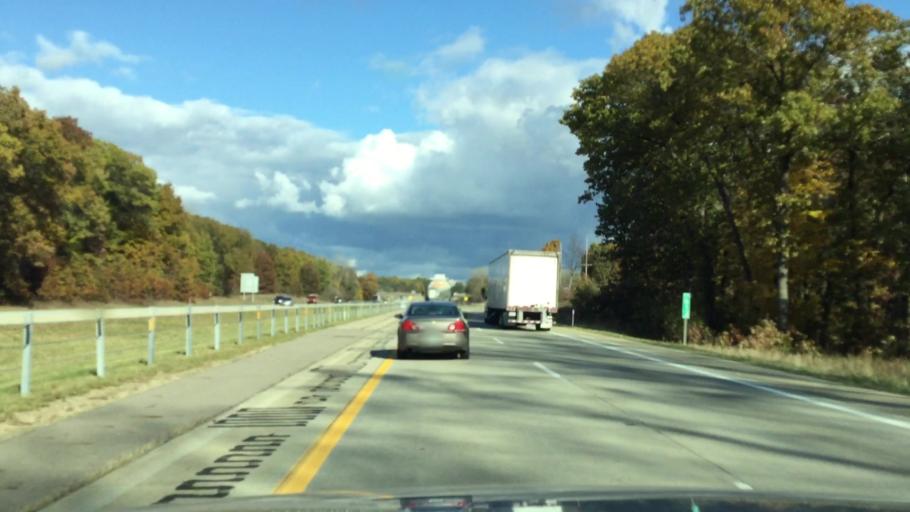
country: US
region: Michigan
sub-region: Van Buren County
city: Paw Paw
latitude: 42.2114
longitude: -85.8698
